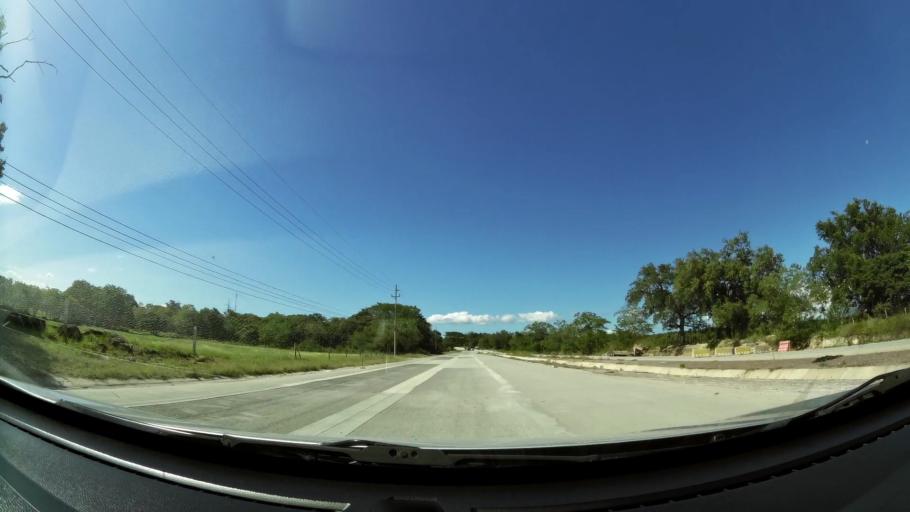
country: CR
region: Guanacaste
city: Liberia
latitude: 10.5588
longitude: -85.3781
